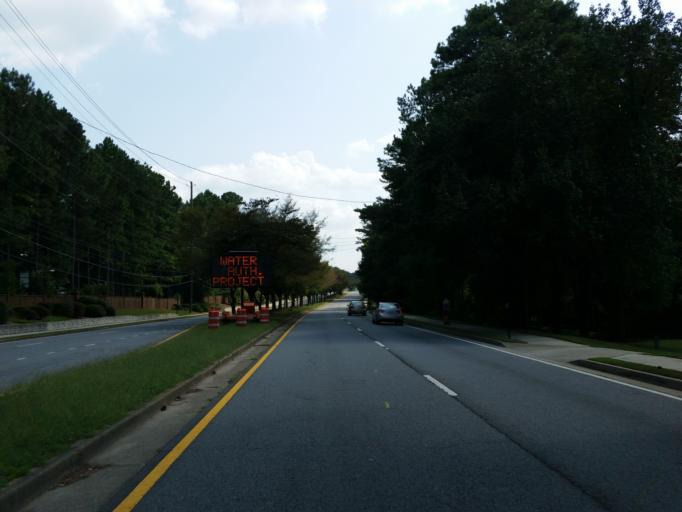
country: US
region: Georgia
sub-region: Cobb County
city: Vinings
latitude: 33.9360
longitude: -84.4610
